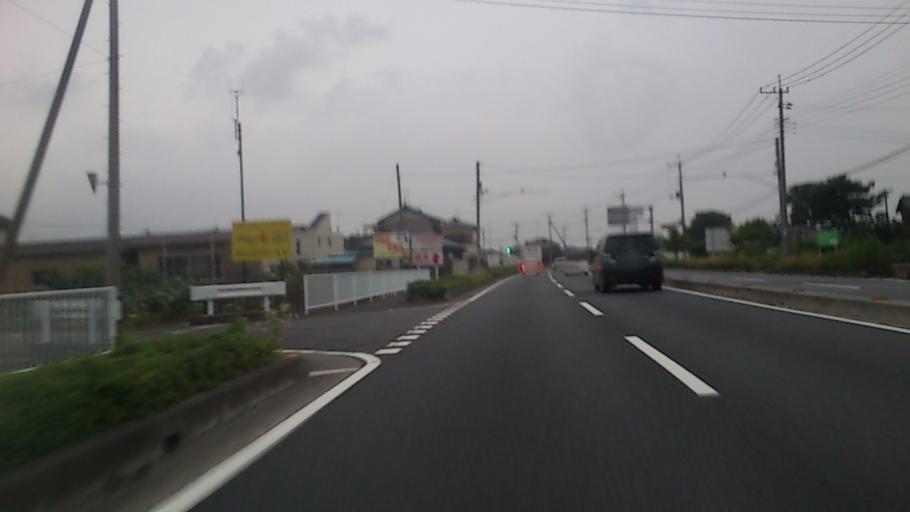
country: JP
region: Saitama
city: Hanyu
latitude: 36.1676
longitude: 139.5819
